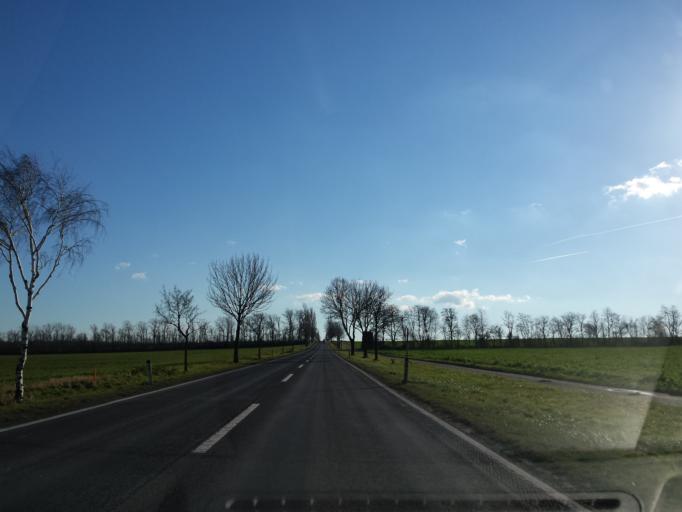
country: AT
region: Lower Austria
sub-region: Politischer Bezirk Wien-Umgebung
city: Rauchenwarth
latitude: 48.1116
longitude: 16.5233
